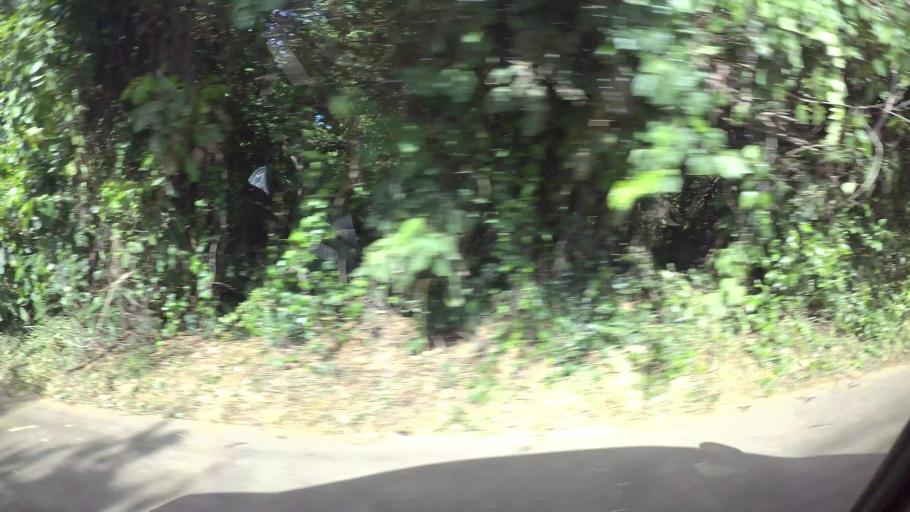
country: TH
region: Chon Buri
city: Sattahip
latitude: 12.6816
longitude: 100.9130
